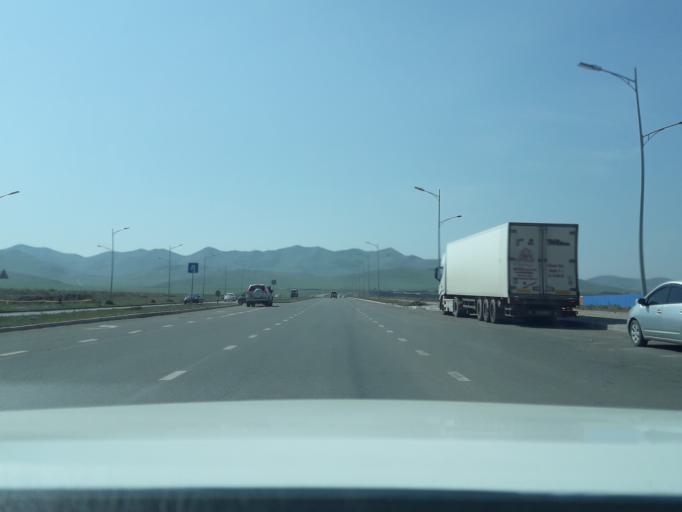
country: MN
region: Ulaanbaatar
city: Ulaanbaatar
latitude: 47.8393
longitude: 106.7897
